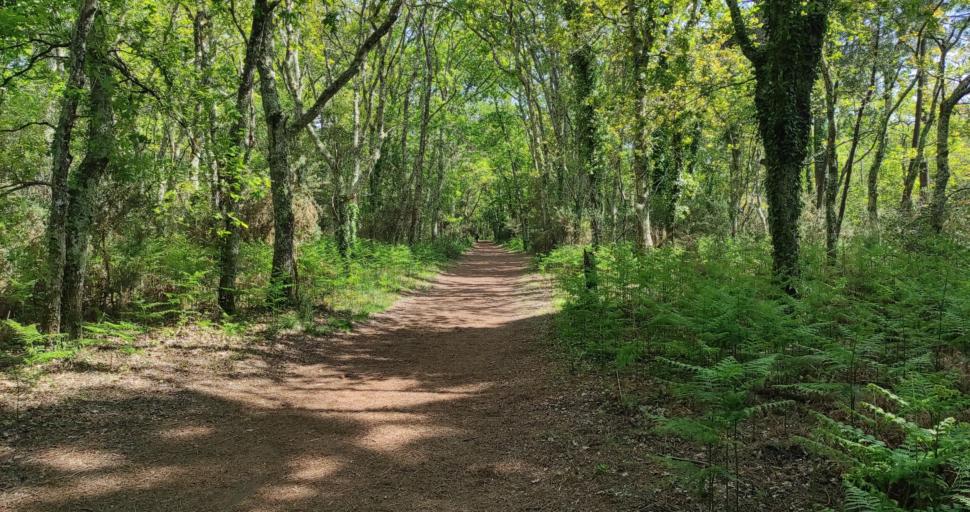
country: FR
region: Aquitaine
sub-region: Departement de la Gironde
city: Andernos-les-Bains
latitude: 44.7480
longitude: -1.1131
